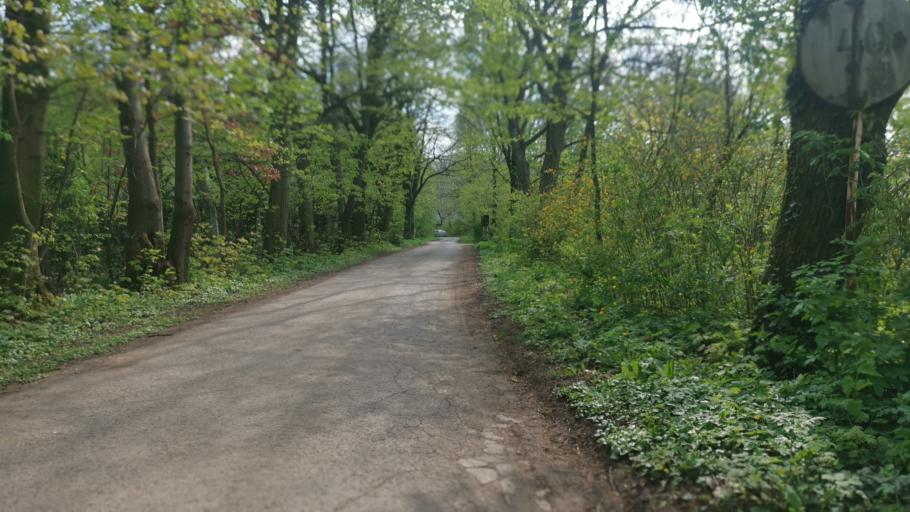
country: SK
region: Trnavsky
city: Smolenice
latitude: 48.5304
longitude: 17.3690
